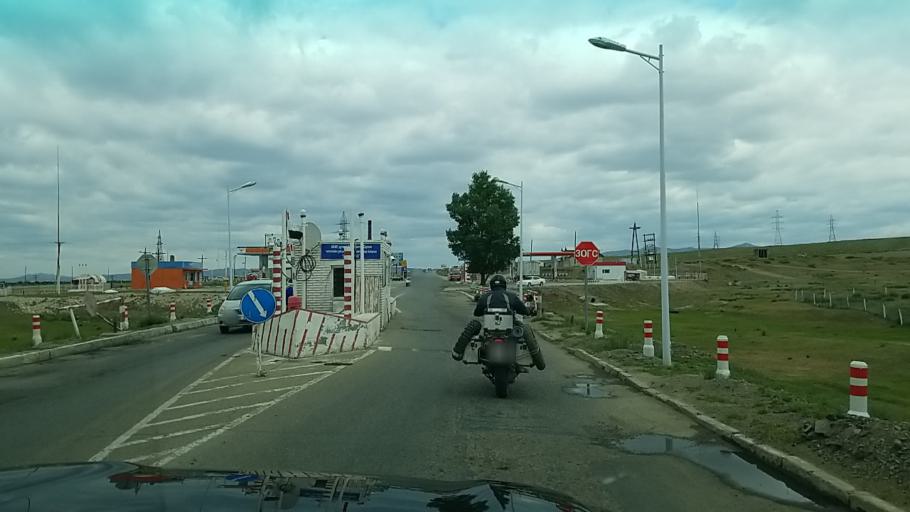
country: MN
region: Darhan Uul
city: Darhan
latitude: 49.3773
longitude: 105.9146
